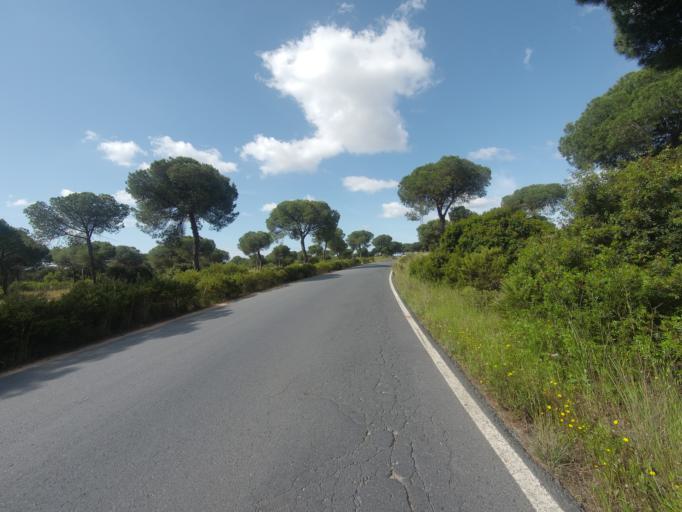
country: ES
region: Andalusia
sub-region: Provincia de Huelva
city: Aljaraque
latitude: 37.2456
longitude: -7.0290
